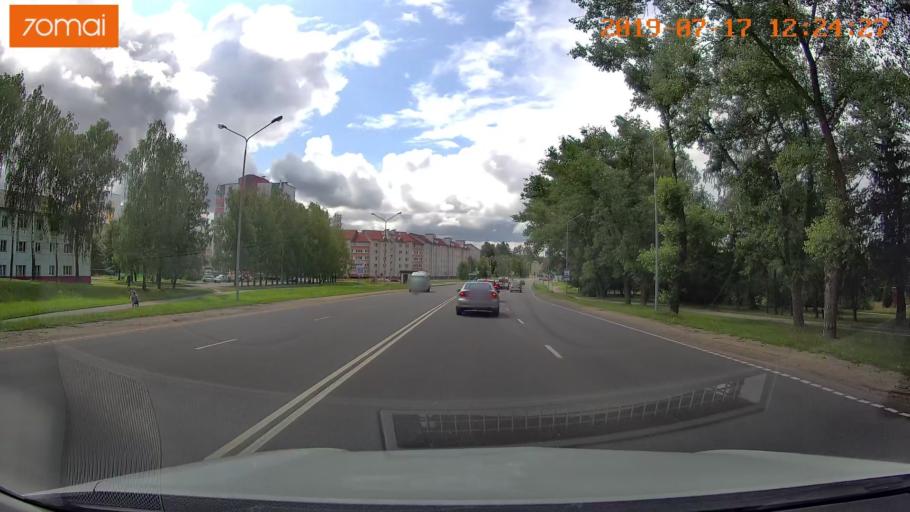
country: BY
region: Minsk
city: Borovlyany
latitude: 53.9937
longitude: 27.6715
